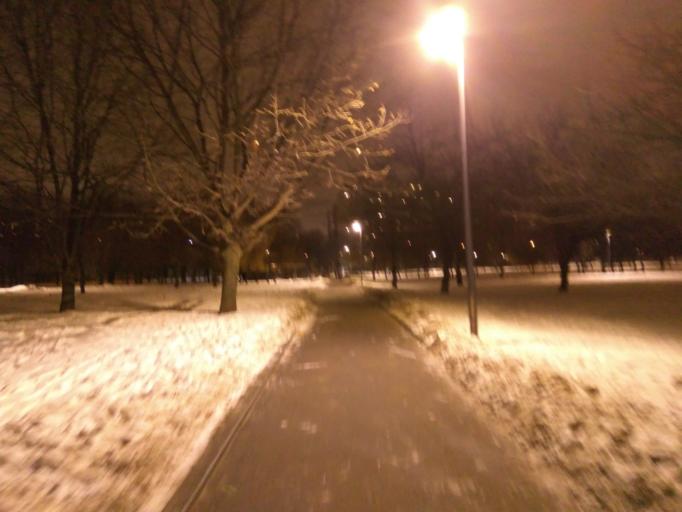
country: RU
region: Moscow
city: Kolomenskoye
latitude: 55.6615
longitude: 37.6495
